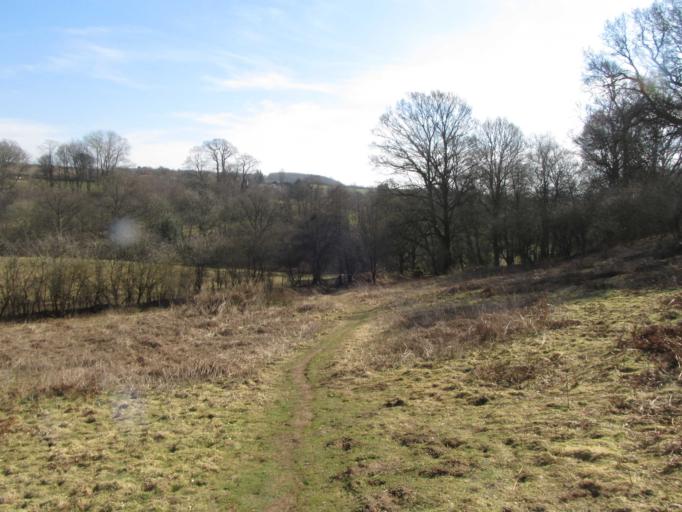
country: GB
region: England
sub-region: West Sussex
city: Petworth
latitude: 50.9825
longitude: -0.6009
